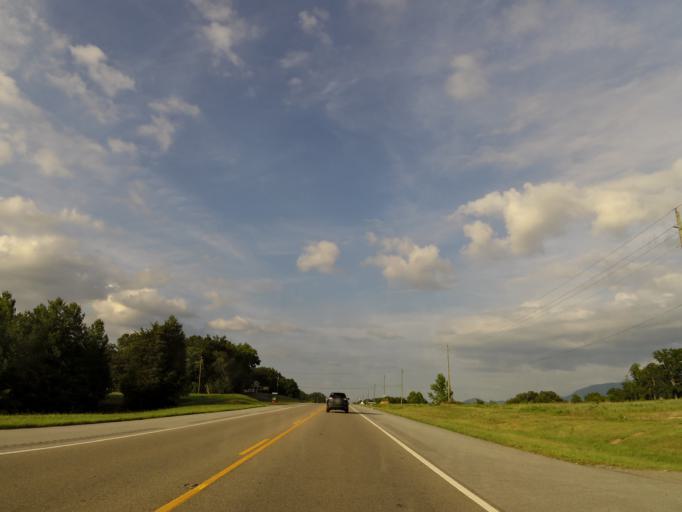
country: US
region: Tennessee
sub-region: Jefferson County
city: Dandridge
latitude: 35.9015
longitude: -83.4236
